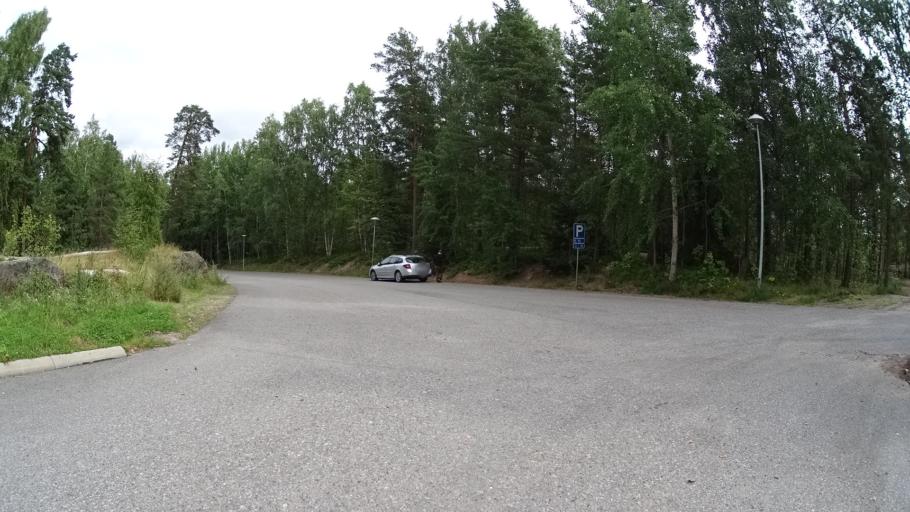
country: FI
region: Uusimaa
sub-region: Helsinki
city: Koukkuniemi
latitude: 60.1614
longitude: 24.7657
